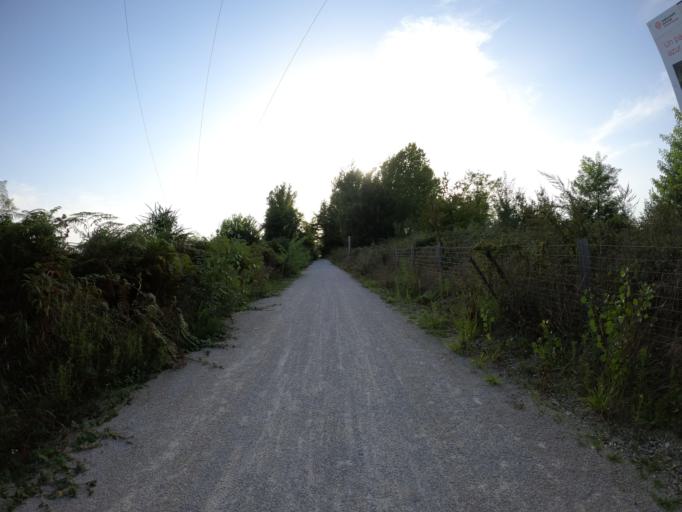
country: FR
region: Midi-Pyrenees
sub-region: Departement de la Haute-Garonne
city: Vieille-Toulouse
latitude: 43.5458
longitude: 1.4267
